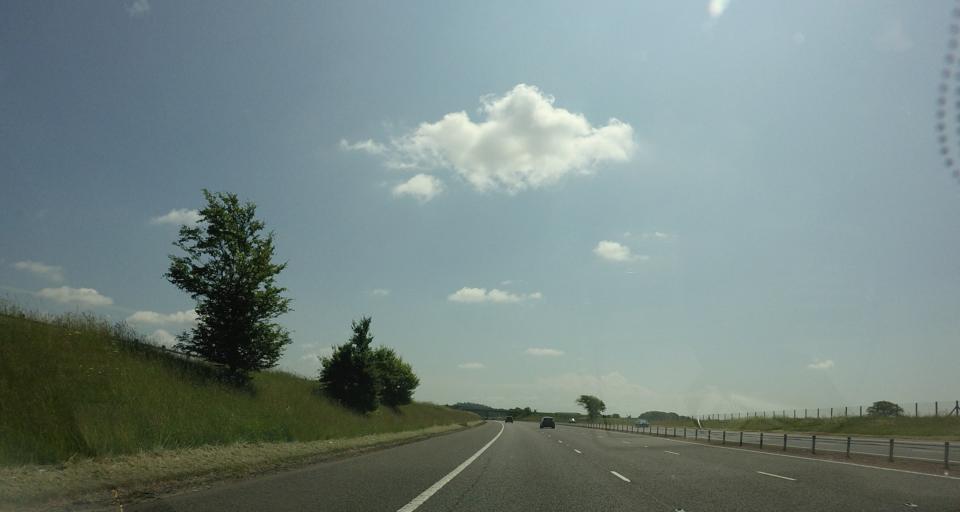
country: GB
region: Scotland
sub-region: Dumfries and Galloway
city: Lockerbie
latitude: 55.1070
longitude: -3.3526
